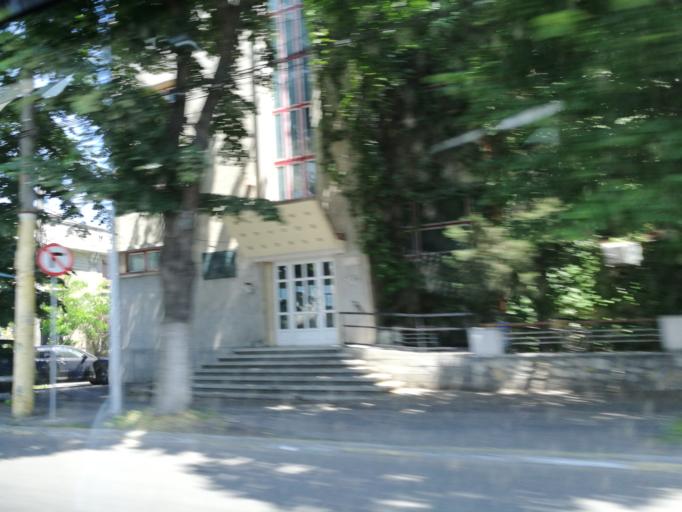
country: RO
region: Constanta
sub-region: Municipiul Constanta
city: Constanta
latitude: 44.1948
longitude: 28.6494
